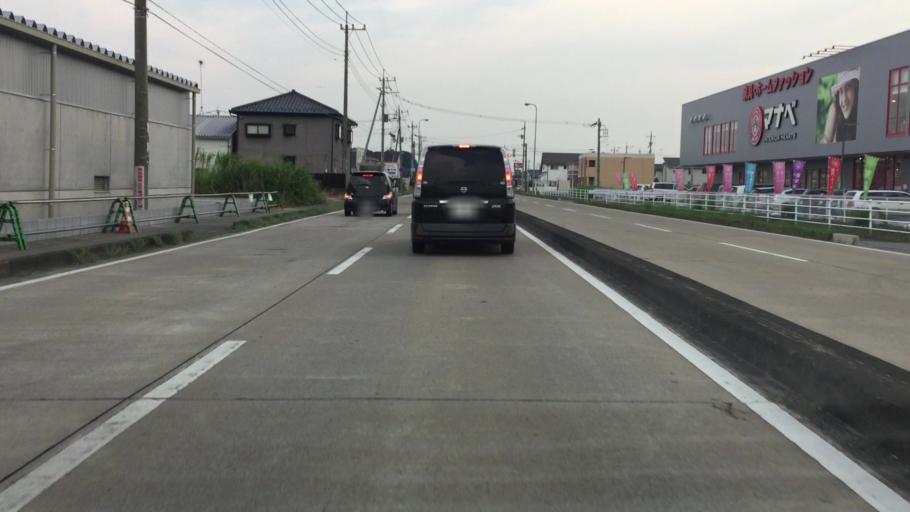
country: JP
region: Tochigi
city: Tochigi
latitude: 36.3461
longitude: 139.7022
